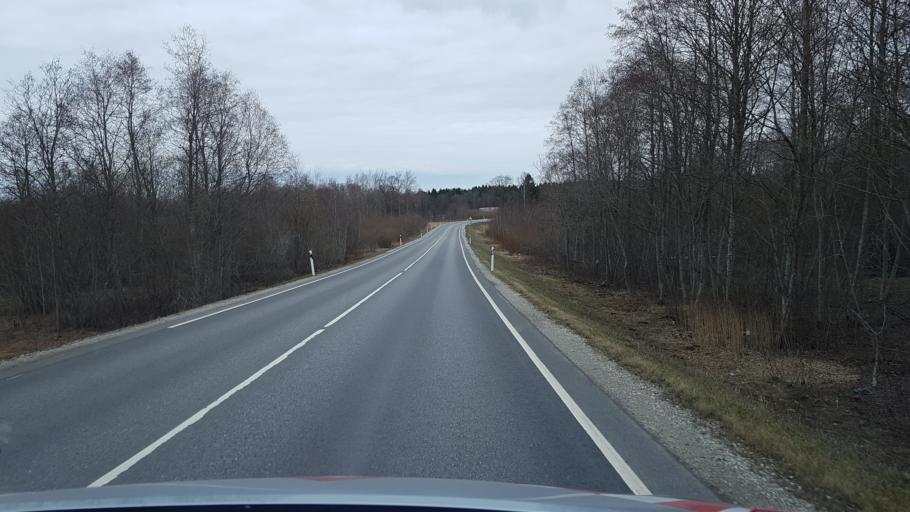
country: EE
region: Ida-Virumaa
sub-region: Narva-Joesuu linn
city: Narva-Joesuu
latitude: 59.4084
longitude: 28.0675
